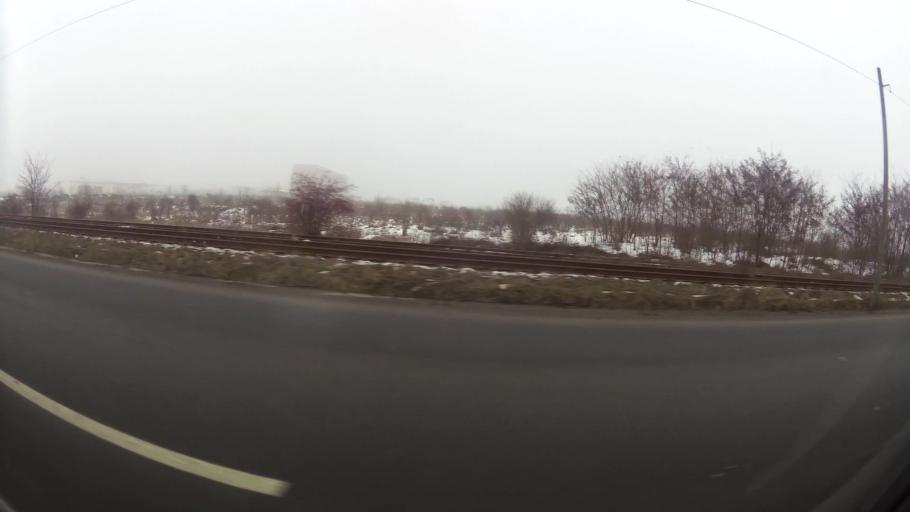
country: RO
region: Ilfov
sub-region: Comuna Bragadiru
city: Bragadiru
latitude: 44.3973
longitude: 25.9812
